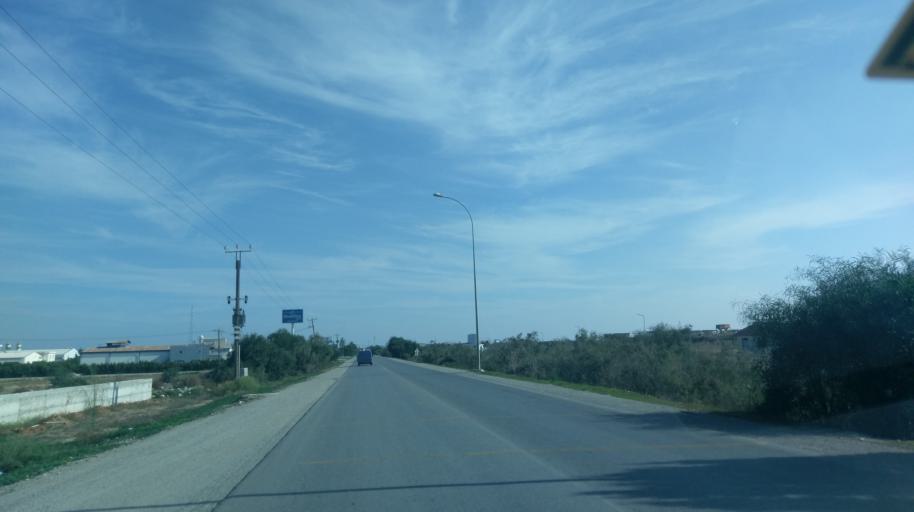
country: CY
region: Ammochostos
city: Acheritou
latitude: 35.1470
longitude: 33.8860
